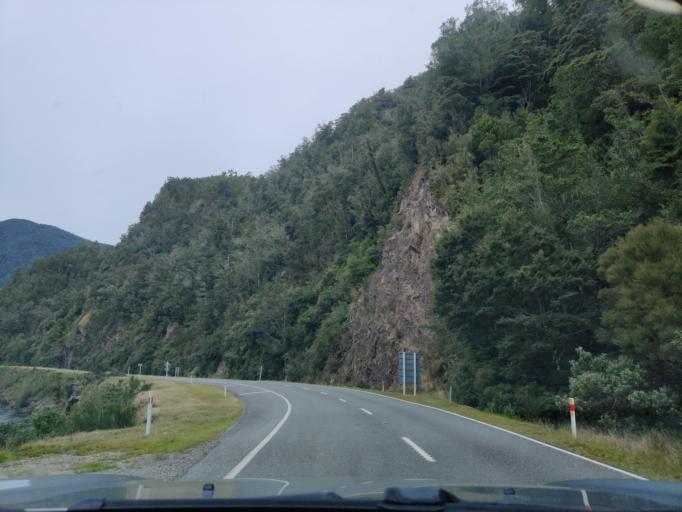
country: NZ
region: West Coast
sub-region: Buller District
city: Westport
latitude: -41.8493
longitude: 171.7340
